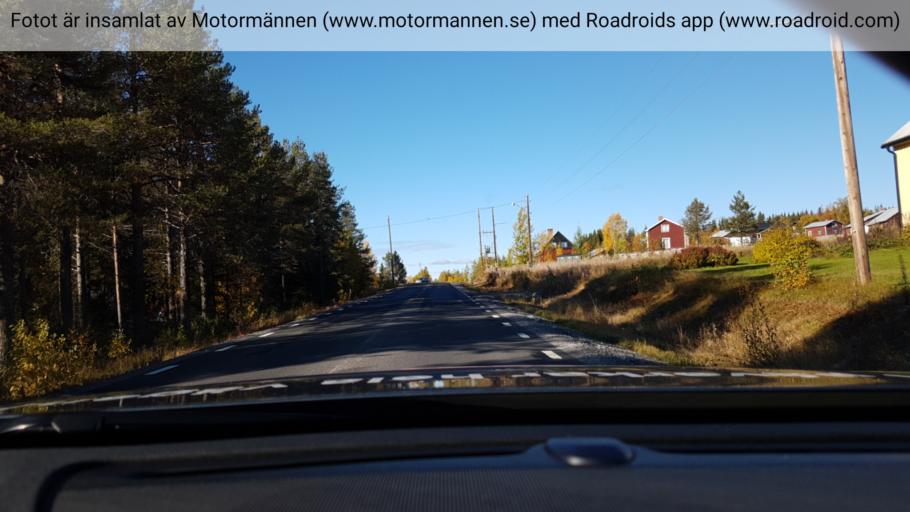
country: SE
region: Norrbotten
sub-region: Gallivare Kommun
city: Gaellivare
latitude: 66.8436
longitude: 21.0162
